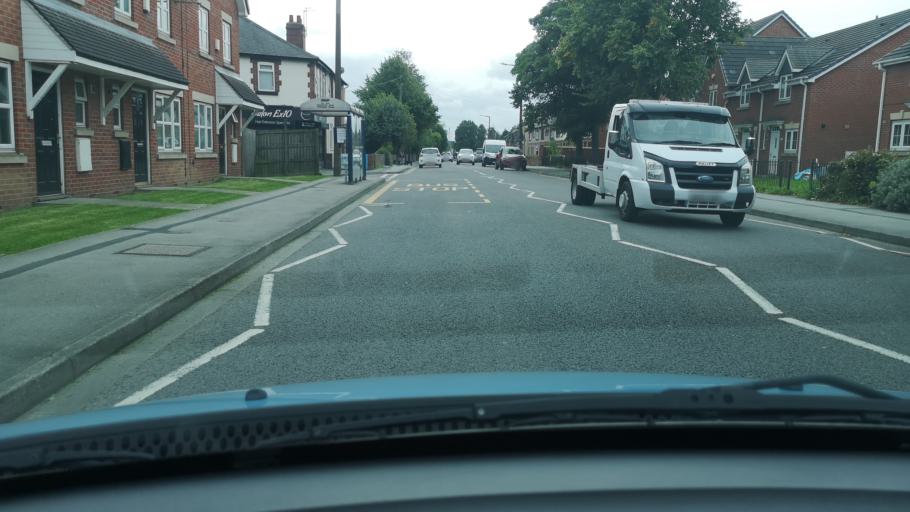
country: GB
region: England
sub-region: Barnsley
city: Shafton
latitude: 53.5837
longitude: -1.4120
